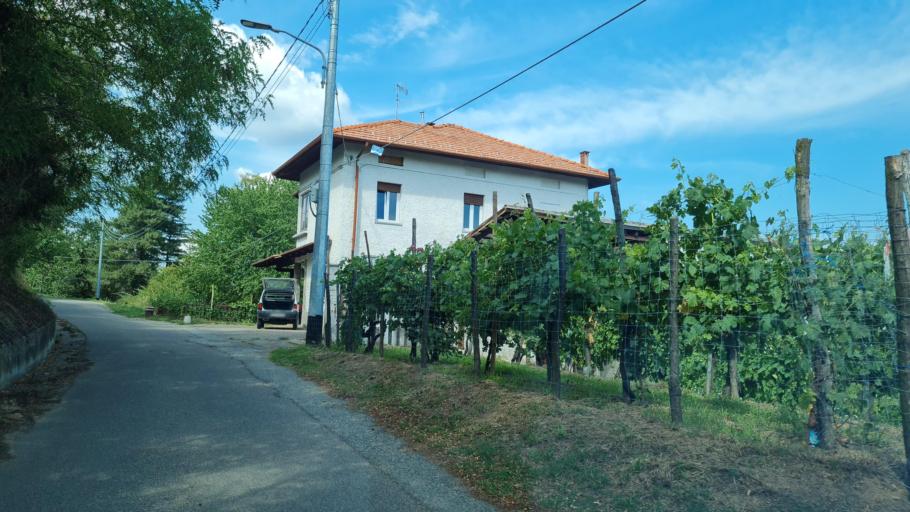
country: IT
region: Piedmont
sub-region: Provincia di Biella
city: Lessona
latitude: 45.5962
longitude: 8.2039
